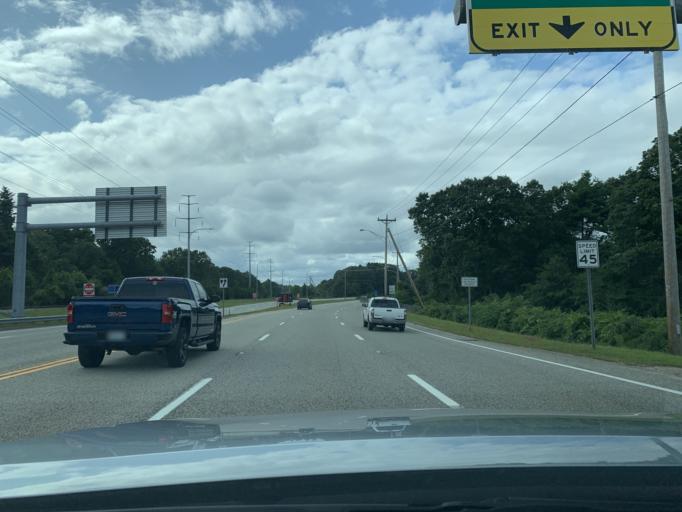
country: US
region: Rhode Island
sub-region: Washington County
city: North Kingstown
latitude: 41.5969
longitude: -71.4403
